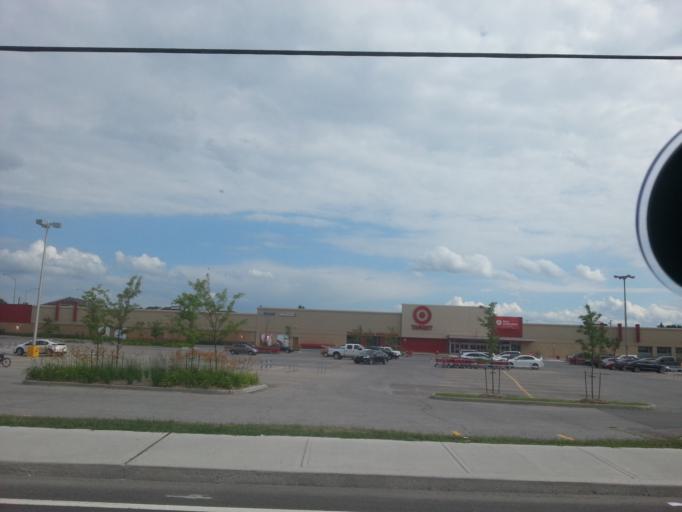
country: CA
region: Quebec
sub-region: Outaouais
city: Gatineau
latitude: 45.4795
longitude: -75.6891
